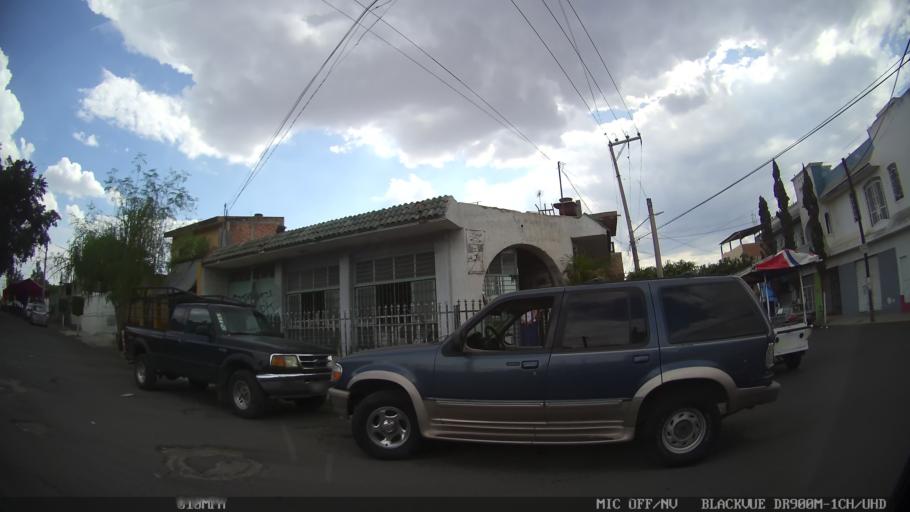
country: MX
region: Jalisco
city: Tlaquepaque
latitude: 20.6326
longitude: -103.2767
